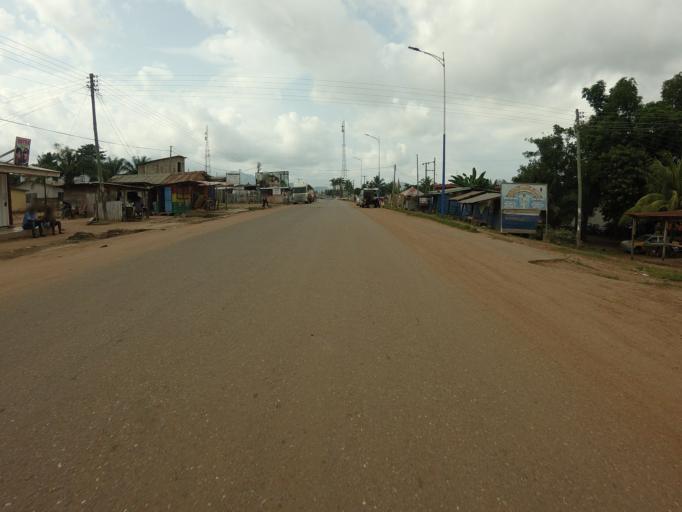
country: GH
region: Volta
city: Hohoe
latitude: 7.1425
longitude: 0.4639
